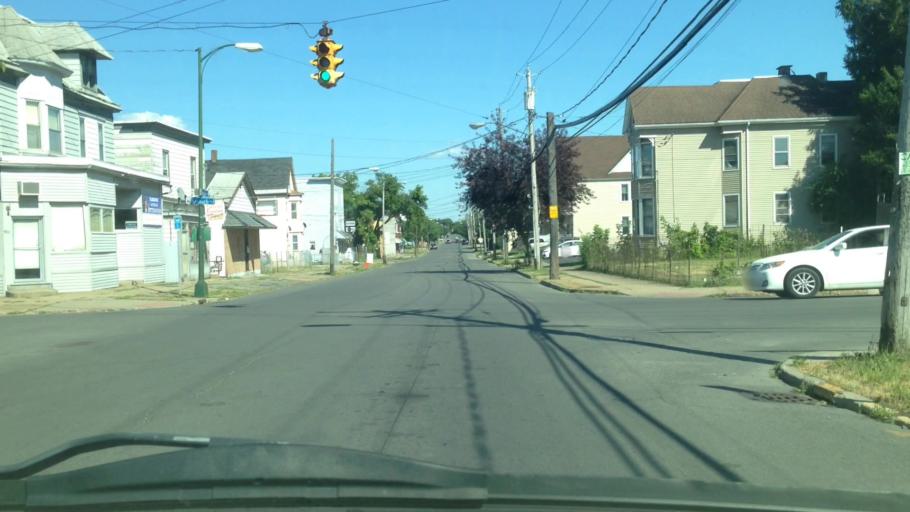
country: US
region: New York
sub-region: Oneida County
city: Utica
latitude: 43.0963
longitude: -75.2115
